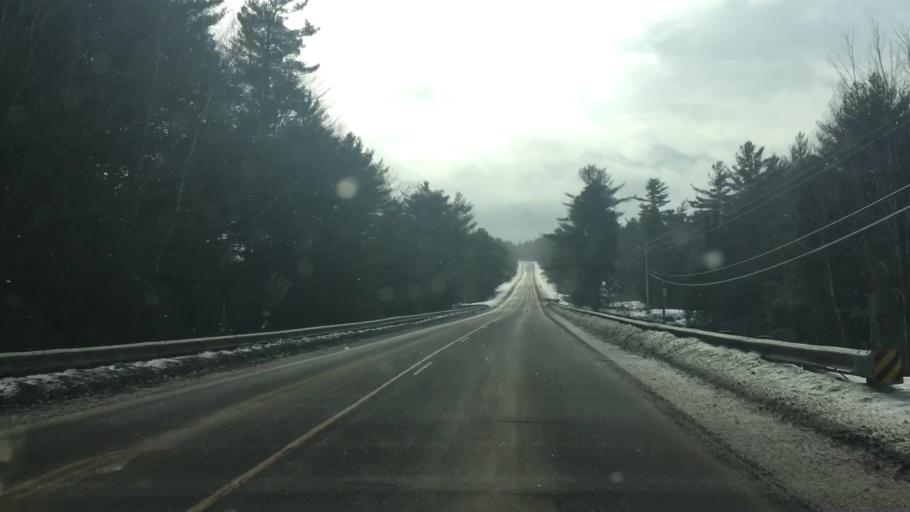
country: US
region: Maine
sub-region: Washington County
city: Calais
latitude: 45.0747
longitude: -67.3322
